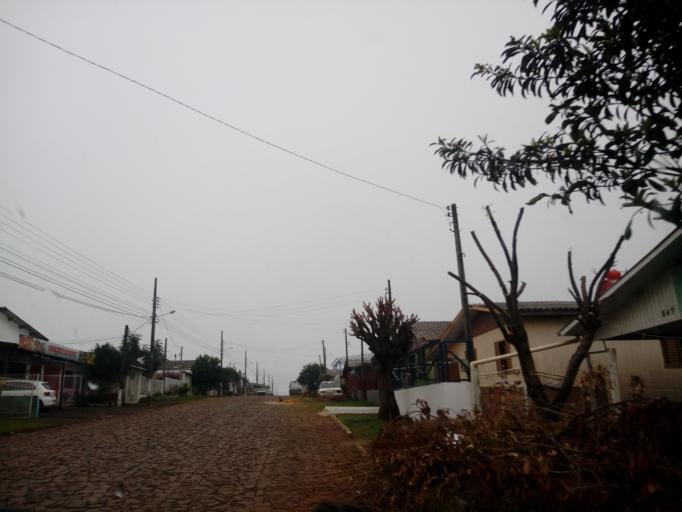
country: BR
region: Santa Catarina
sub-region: Chapeco
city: Chapeco
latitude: -27.1073
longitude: -52.6758
